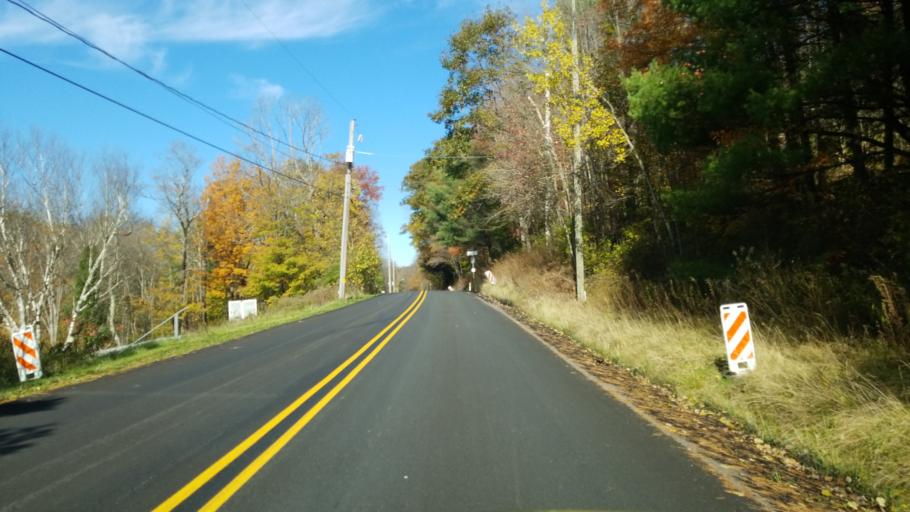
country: US
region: Pennsylvania
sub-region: Jefferson County
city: Brockway
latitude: 41.2406
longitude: -78.7965
